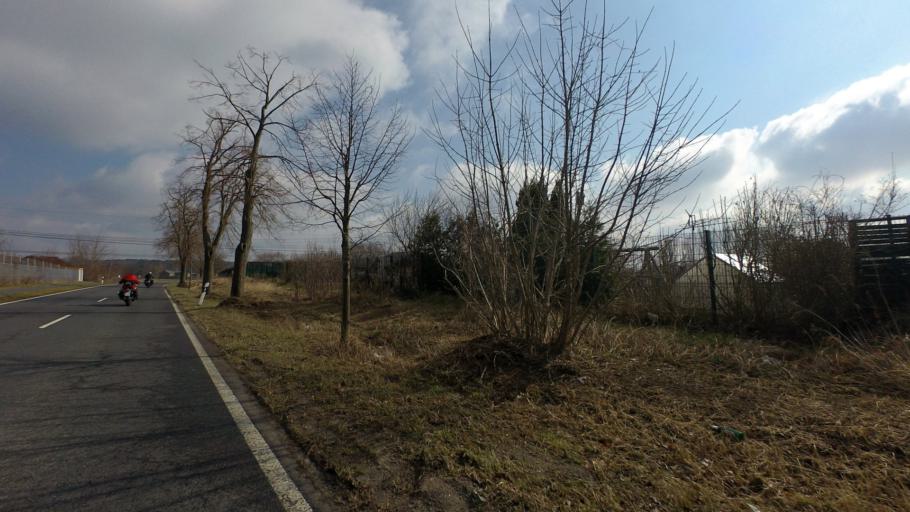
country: DE
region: Berlin
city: Blankenfelde
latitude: 52.6686
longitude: 13.3909
